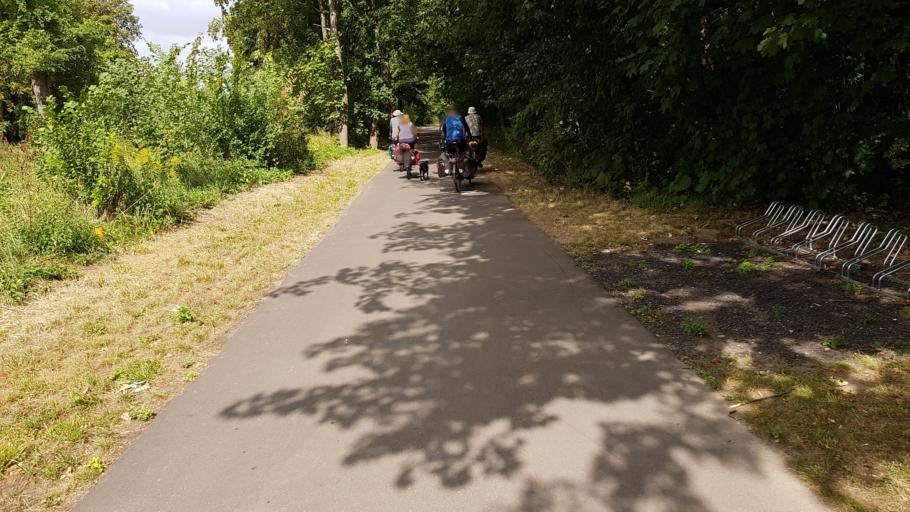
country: PL
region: West Pomeranian Voivodeship
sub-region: Powiat pyrzycki
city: Pyrzyce
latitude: 53.1342
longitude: 14.9763
